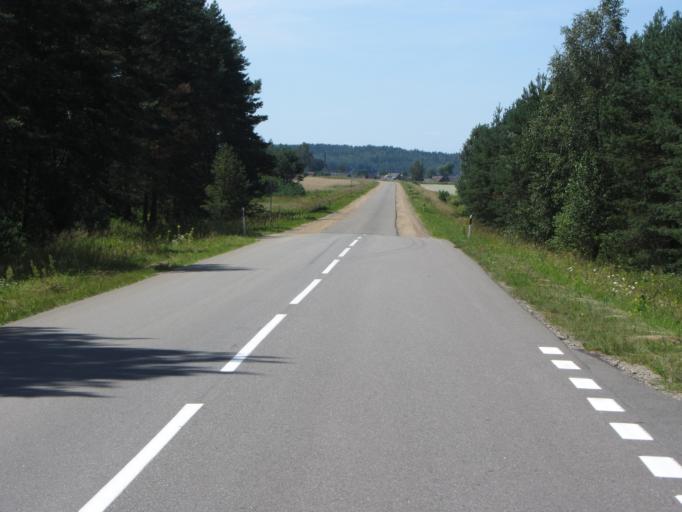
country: LT
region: Vilnius County
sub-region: Trakai
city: Rudiskes
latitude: 54.3052
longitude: 24.8016
